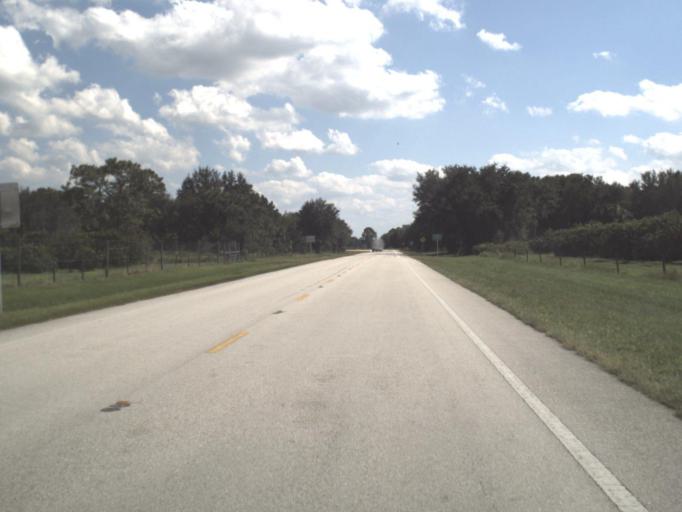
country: US
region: Florida
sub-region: Highlands County
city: Sebring
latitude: 27.4157
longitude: -81.5651
